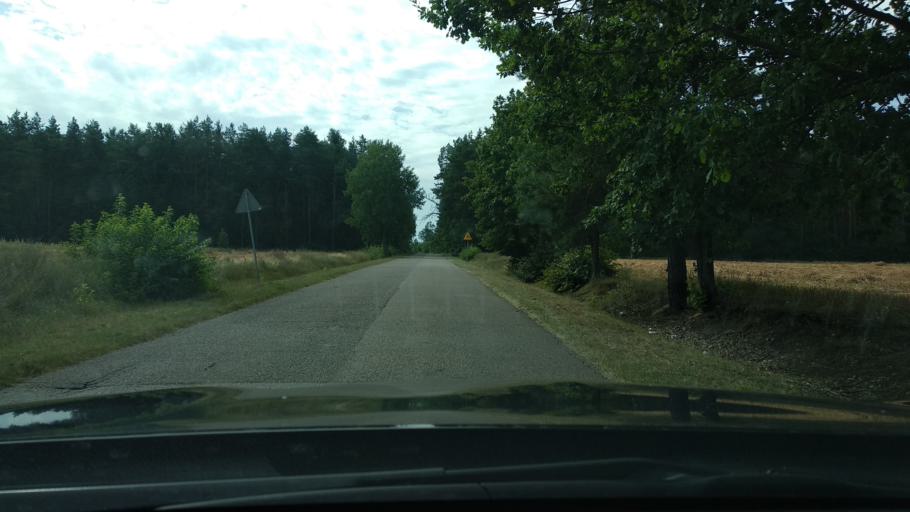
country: PL
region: Masovian Voivodeship
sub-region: Powiat pultuski
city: Zatory
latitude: 52.6423
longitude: 21.1842
